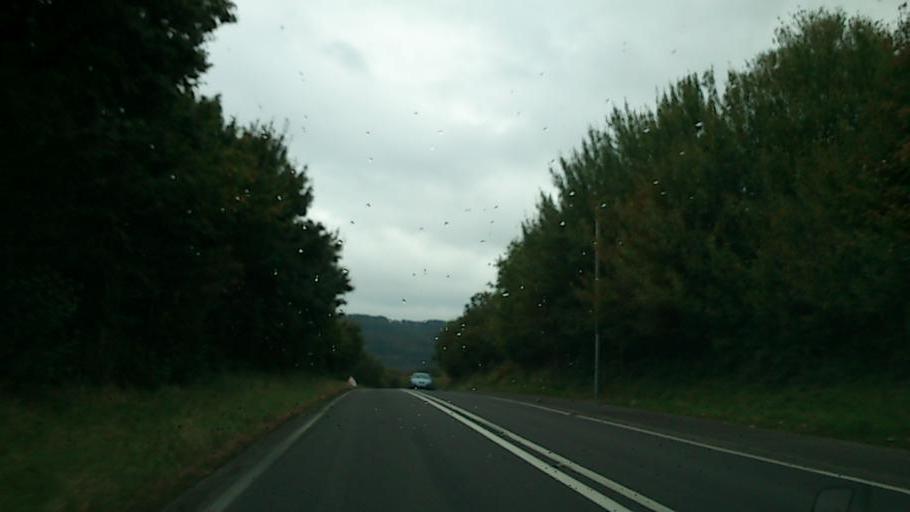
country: GB
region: Wales
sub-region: County of Ceredigion
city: Bow Street
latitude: 52.4641
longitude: -4.0014
